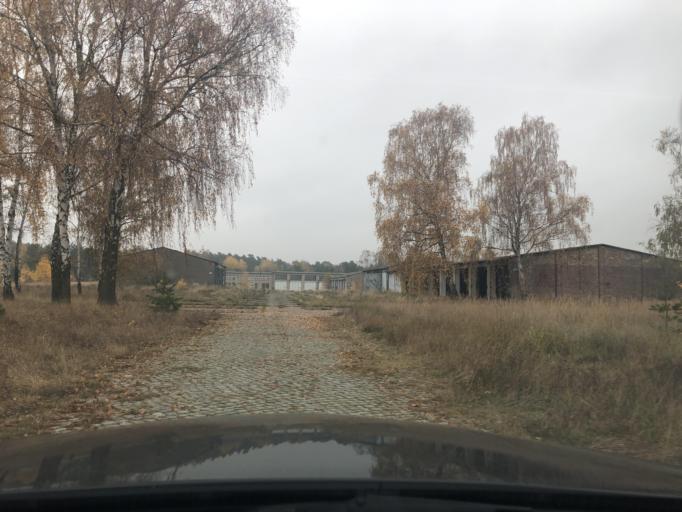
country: DE
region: Mecklenburg-Vorpommern
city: Eggesin
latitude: 53.6639
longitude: 14.1182
